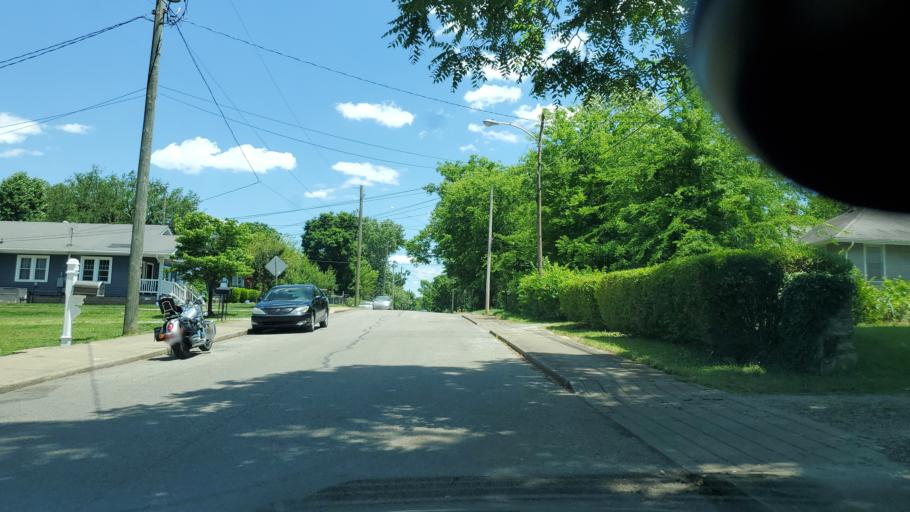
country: US
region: Tennessee
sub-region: Davidson County
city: Nashville
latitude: 36.1899
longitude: -86.7511
